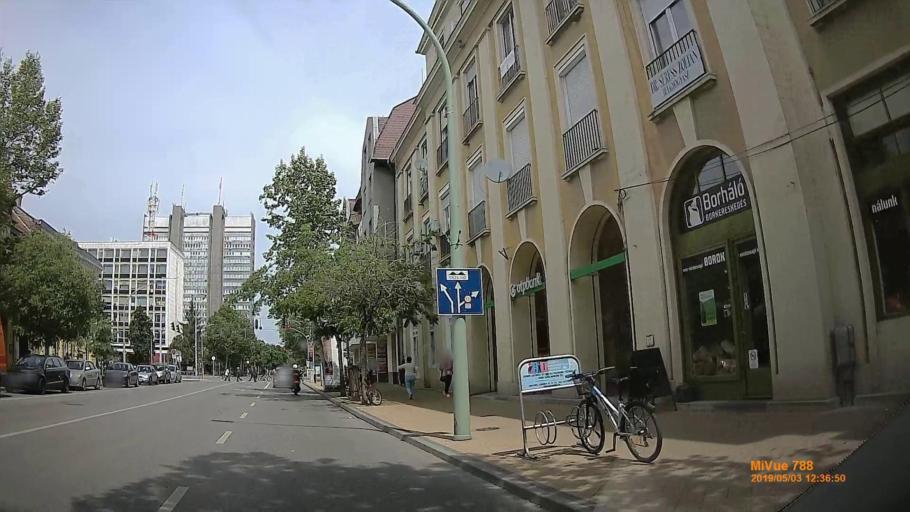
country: HU
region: Jasz-Nagykun-Szolnok
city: Szolnok
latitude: 47.1744
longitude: 20.1938
